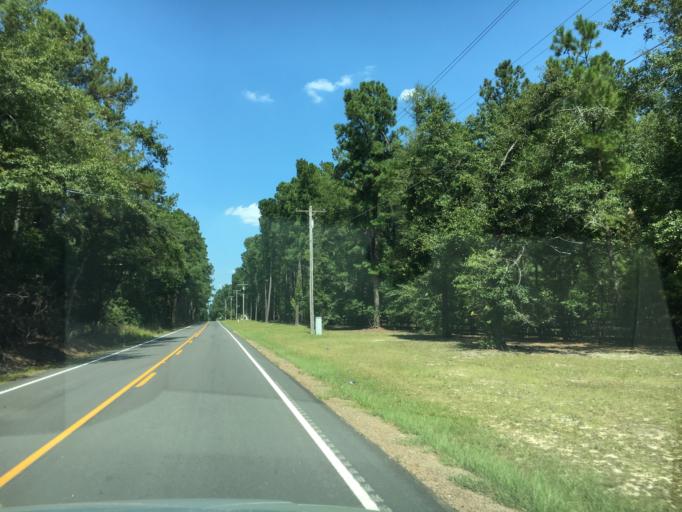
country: US
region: South Carolina
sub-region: Aiken County
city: Aiken
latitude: 33.5049
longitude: -81.6540
